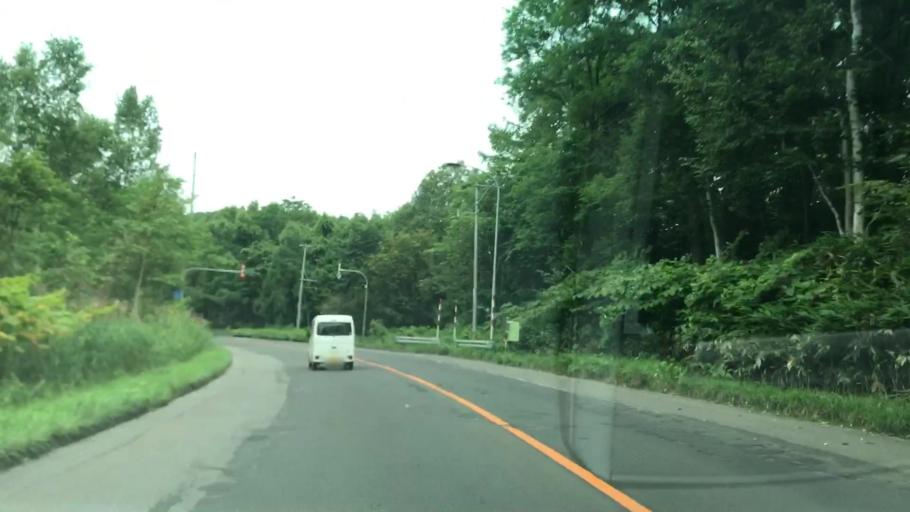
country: JP
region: Hokkaido
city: Niseko Town
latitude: 42.9444
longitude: 140.7053
